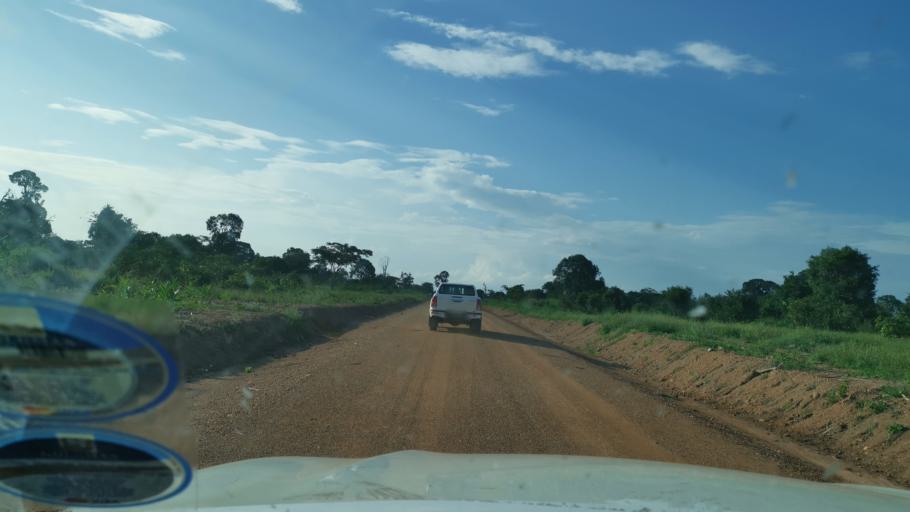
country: ZM
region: Luapula
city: Samfya
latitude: -11.1201
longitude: 29.5806
